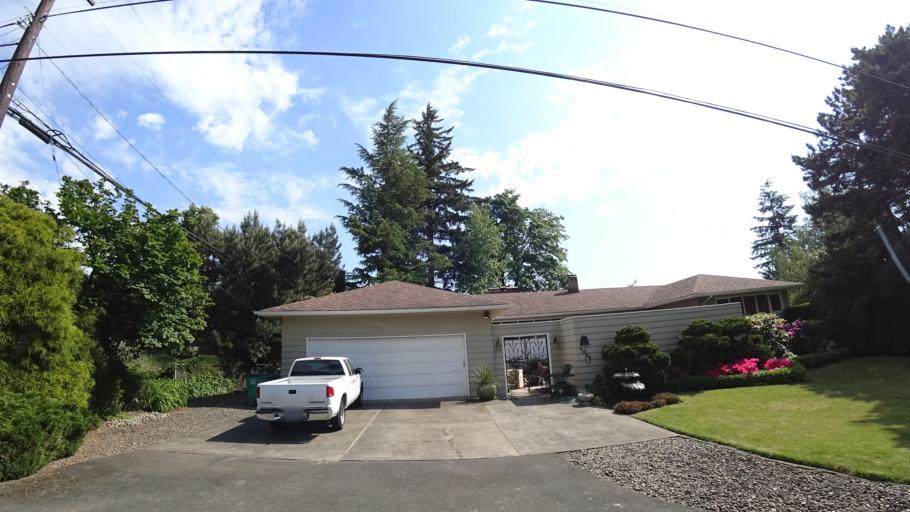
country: US
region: Oregon
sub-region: Washington County
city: Metzger
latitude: 45.4534
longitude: -122.7411
